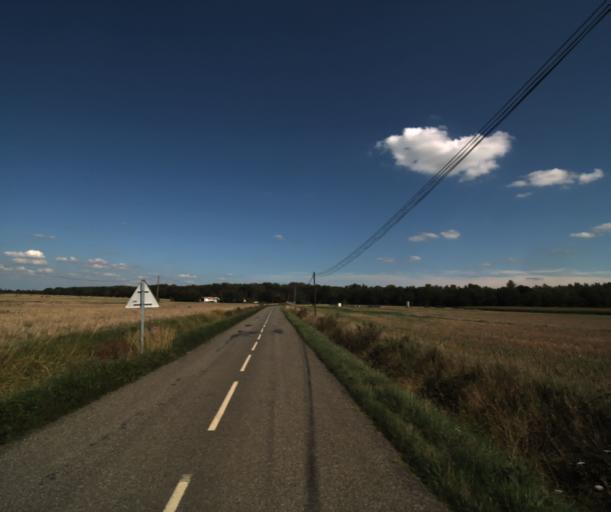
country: FR
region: Midi-Pyrenees
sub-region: Departement de la Haute-Garonne
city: Fonsorbes
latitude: 43.4990
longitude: 1.2217
